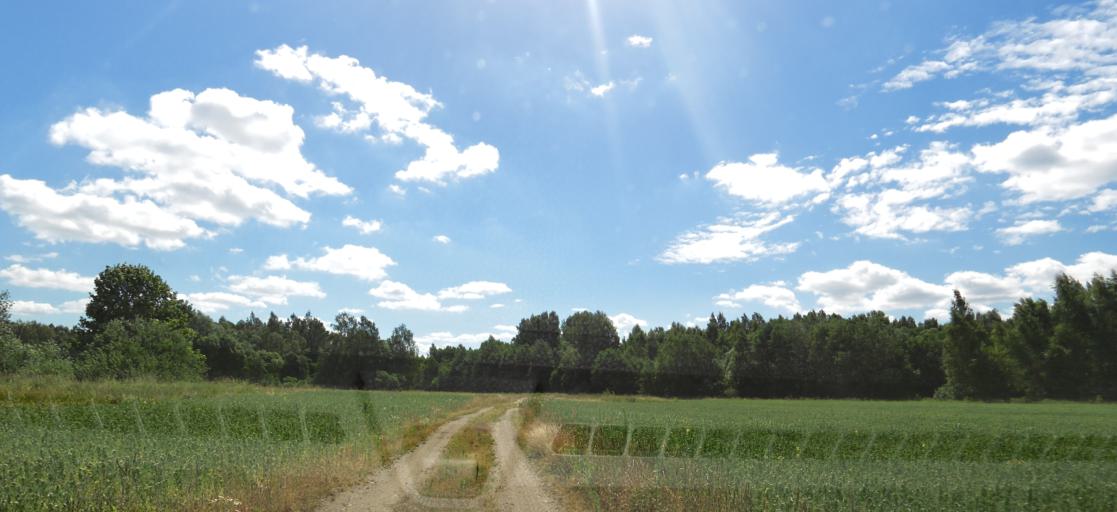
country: LT
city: Vabalninkas
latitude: 56.0303
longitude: 24.9274
